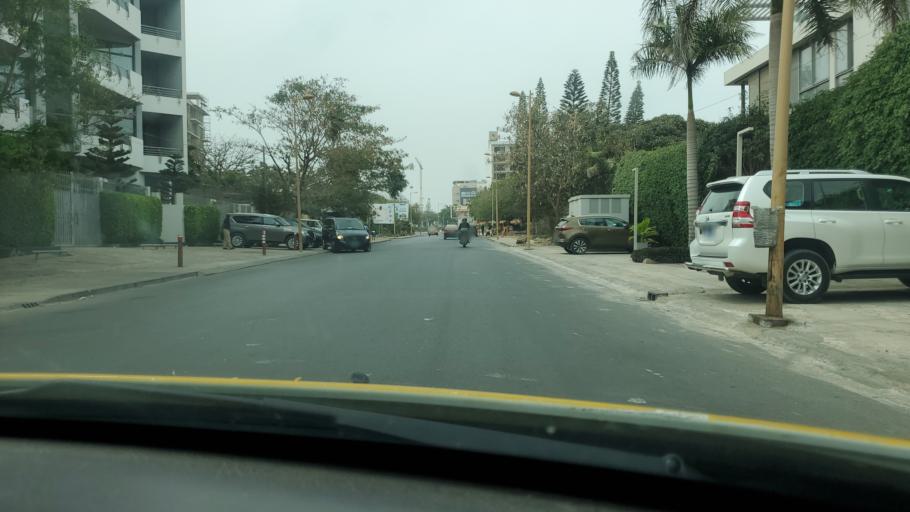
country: SN
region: Dakar
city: Mermoz Boabab
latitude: 14.7015
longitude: -17.4751
